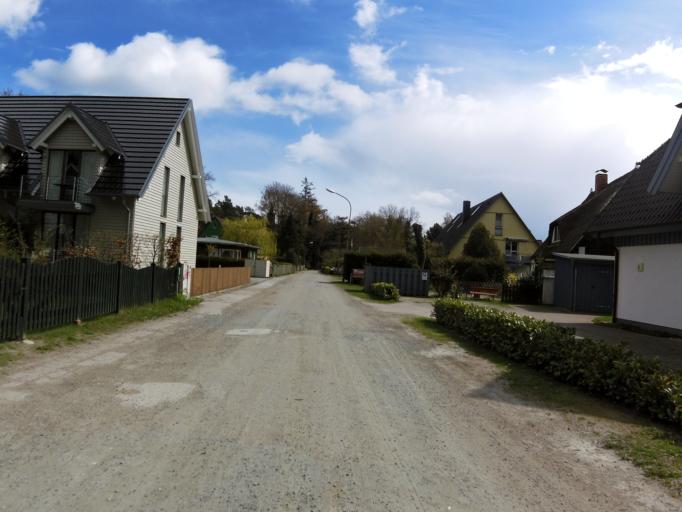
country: DE
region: Mecklenburg-Vorpommern
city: Ostseebad Prerow
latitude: 54.4491
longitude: 12.5625
